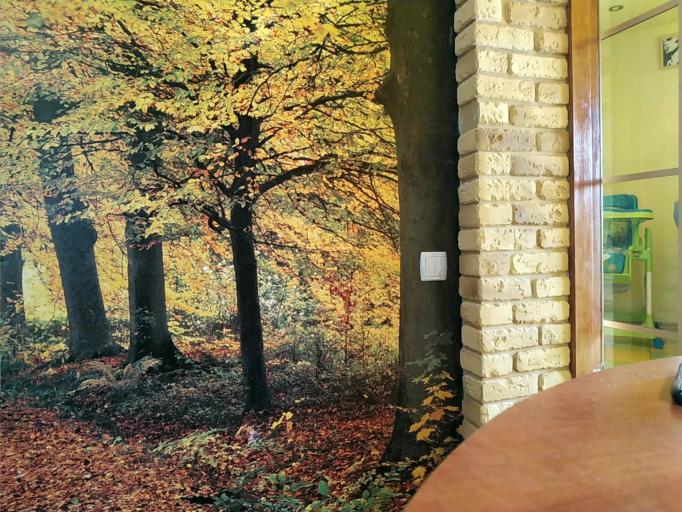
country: RU
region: Novgorod
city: Parfino
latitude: 57.7966
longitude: 31.6277
